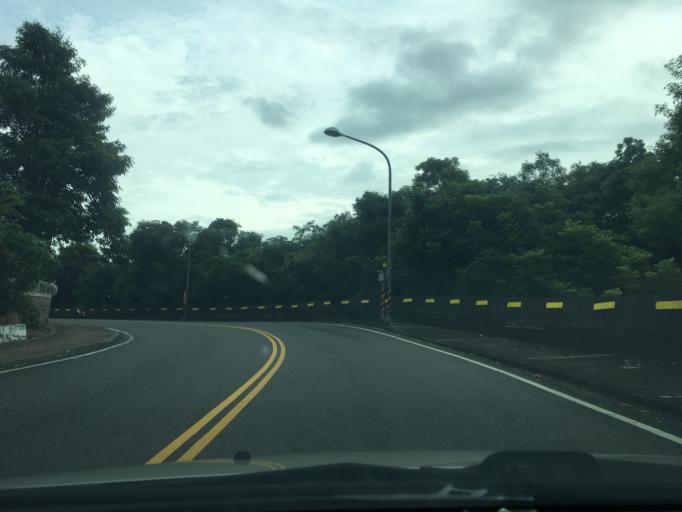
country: TW
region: Taiwan
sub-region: Changhua
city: Chang-hua
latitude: 24.0677
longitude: 120.5658
